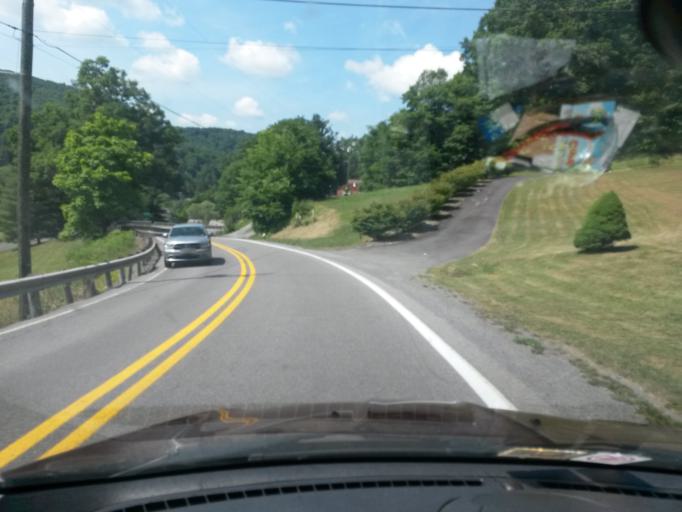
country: US
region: West Virginia
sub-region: Mercer County
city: Princeton
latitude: 37.3864
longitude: -81.1210
